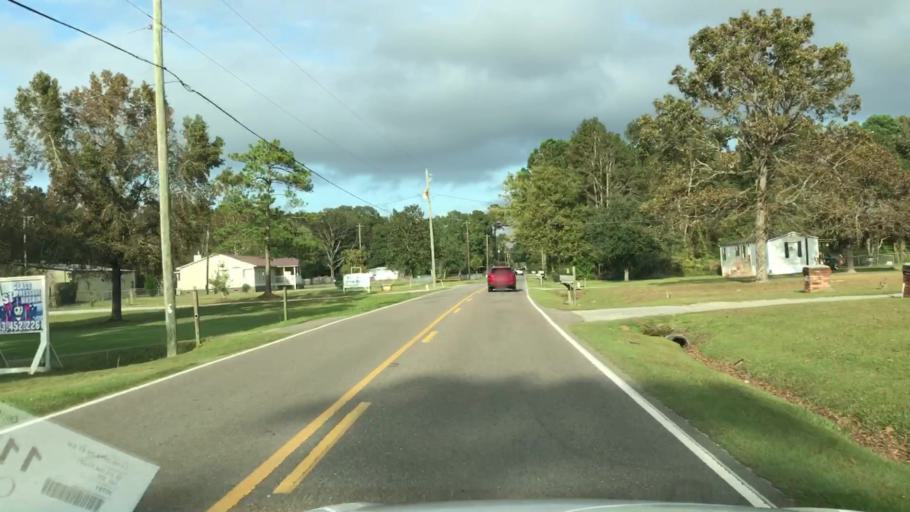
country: US
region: South Carolina
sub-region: Berkeley County
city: Sangaree
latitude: 33.0237
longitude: -80.1199
